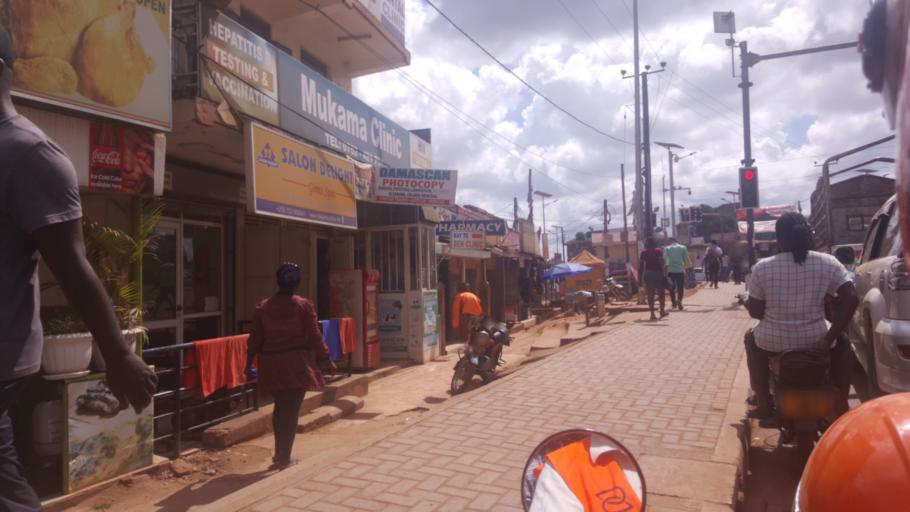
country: UG
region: Central Region
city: Kampala Central Division
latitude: 0.3249
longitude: 32.5601
